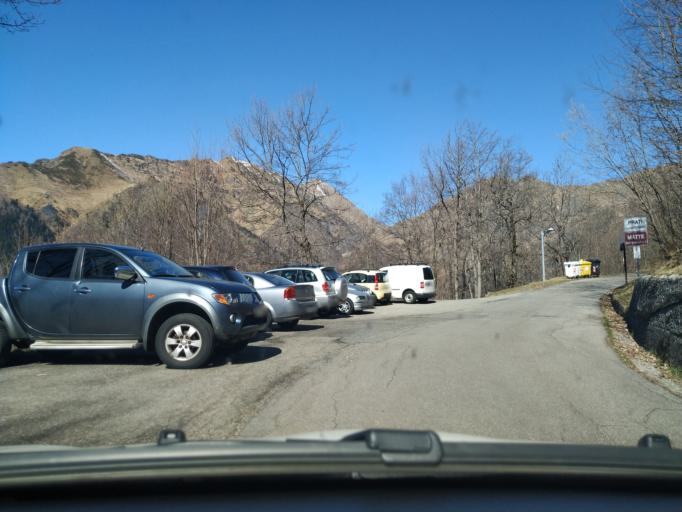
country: IT
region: Piedmont
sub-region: Provincia di Vercelli
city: Rimella
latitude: 45.9069
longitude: 8.1854
